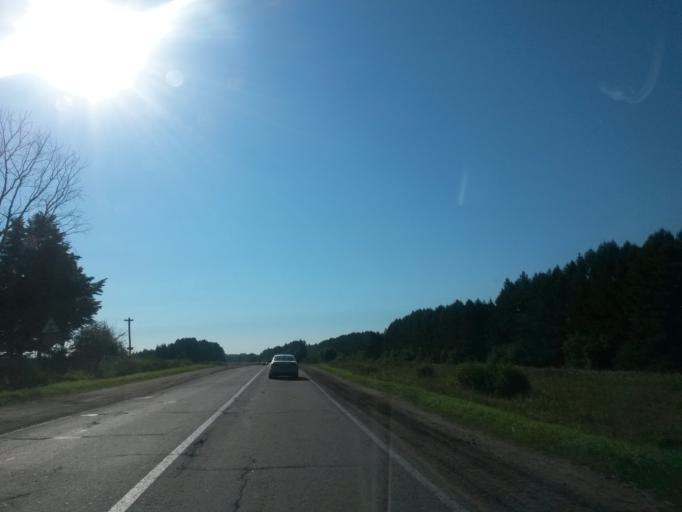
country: RU
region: Jaroslavl
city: Krasnyye Tkachi
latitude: 57.3943
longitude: 39.6777
